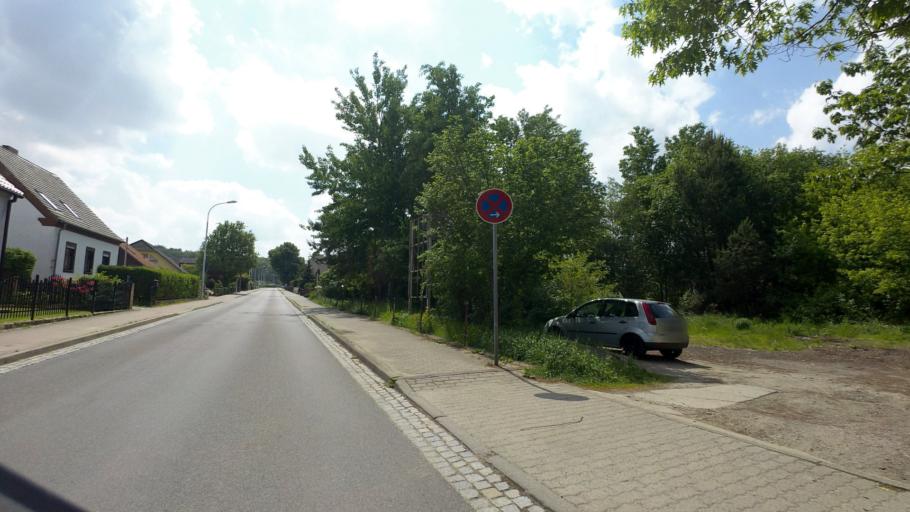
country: DE
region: Saxony
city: Weisswasser
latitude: 51.5071
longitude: 14.6173
